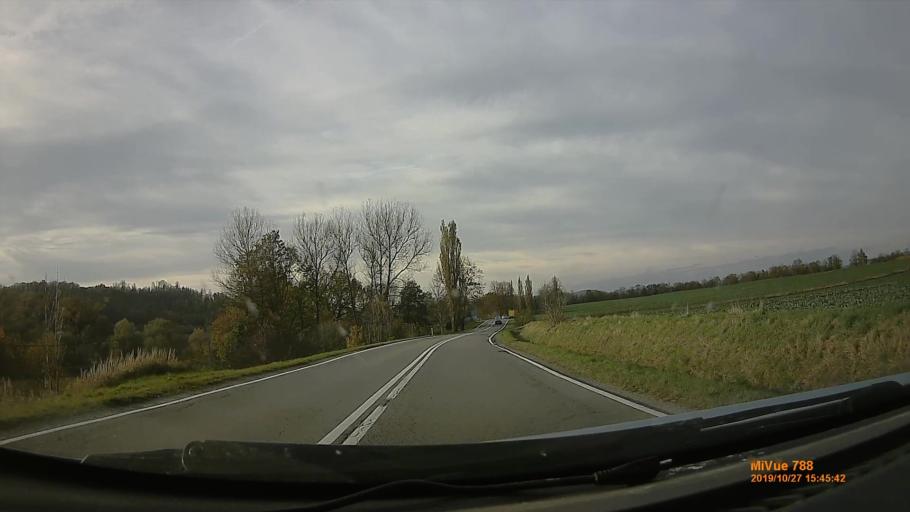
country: PL
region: Lower Silesian Voivodeship
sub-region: Powiat klodzki
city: Bozkow
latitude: 50.4761
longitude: 16.5929
